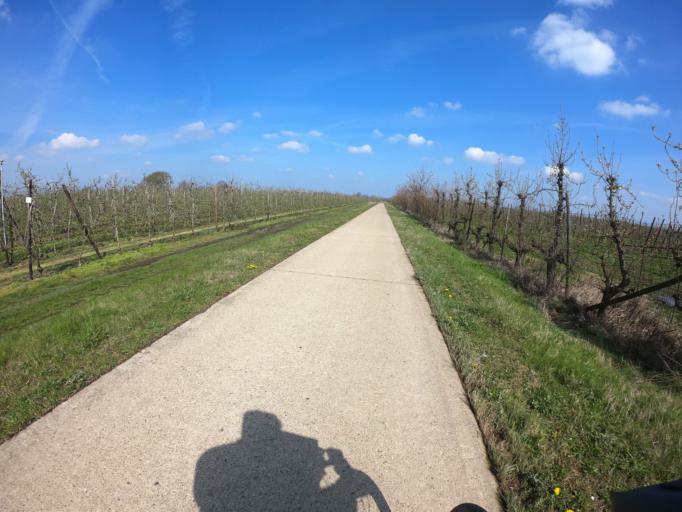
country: BE
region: Flanders
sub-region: Provincie Limburg
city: Halen
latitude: 50.9232
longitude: 5.1125
